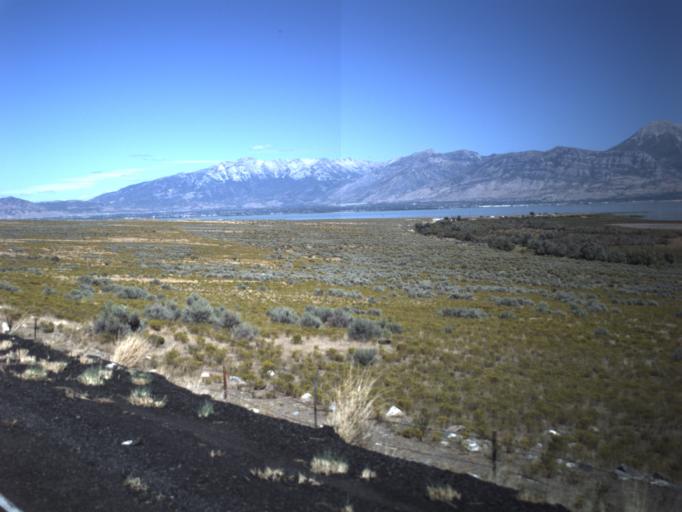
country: US
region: Utah
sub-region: Utah County
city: Saratoga Springs
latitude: 40.2517
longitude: -111.8664
